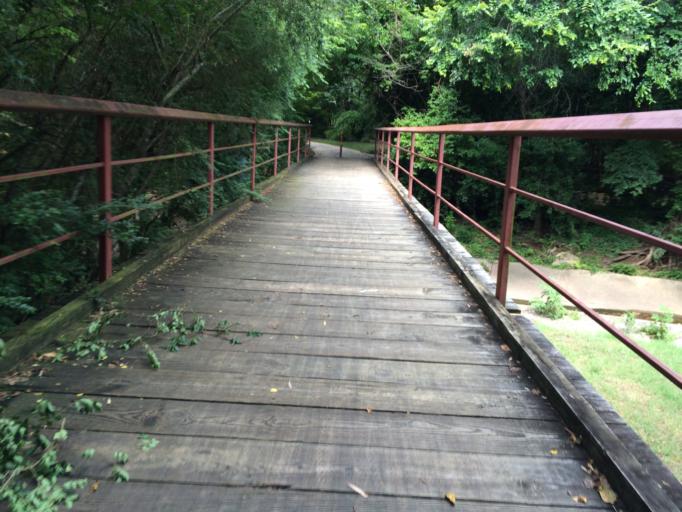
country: US
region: Oklahoma
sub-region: Cleveland County
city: Norman
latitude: 35.2013
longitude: -97.4576
